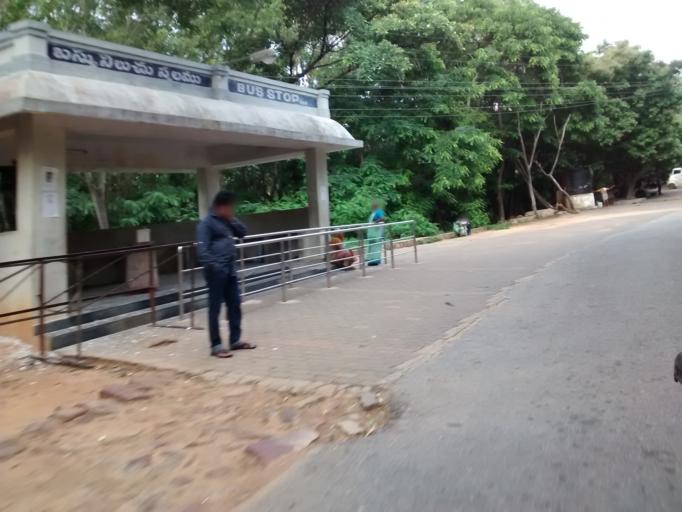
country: IN
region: Andhra Pradesh
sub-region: Chittoor
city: Tirumala
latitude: 13.7048
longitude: 79.3443
